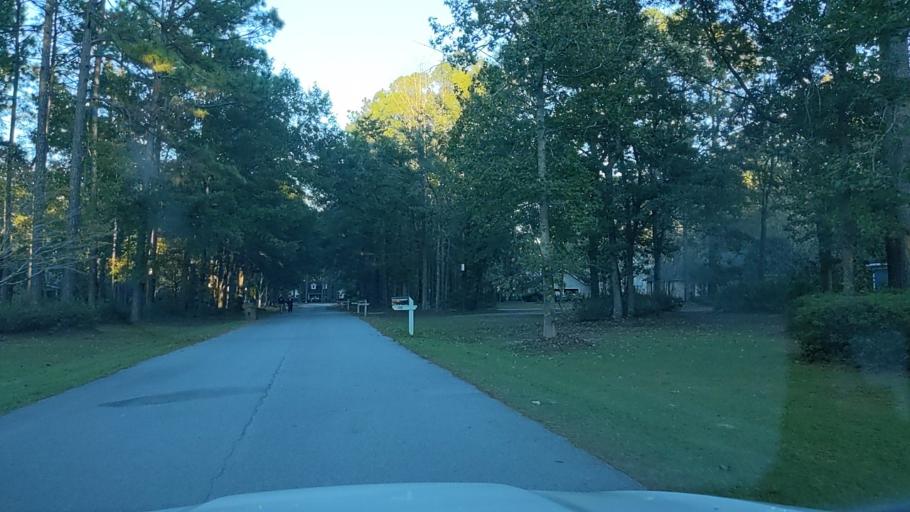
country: US
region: Georgia
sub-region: Effingham County
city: Rincon
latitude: 32.2661
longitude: -81.2087
